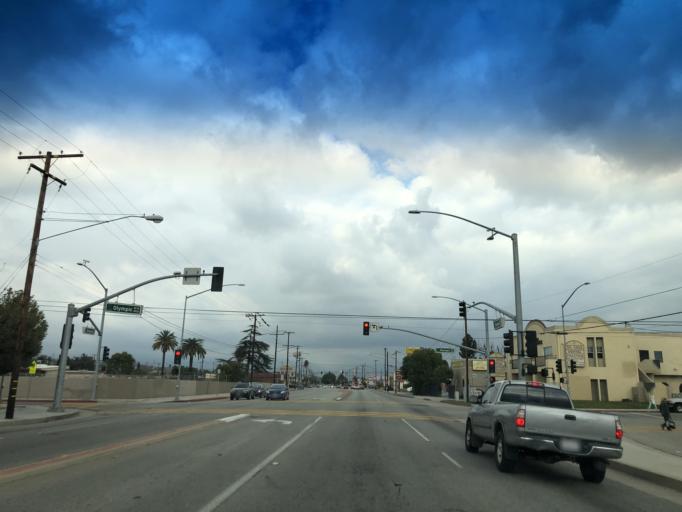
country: US
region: California
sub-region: Los Angeles County
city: Montebello
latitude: 34.0054
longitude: -118.0827
